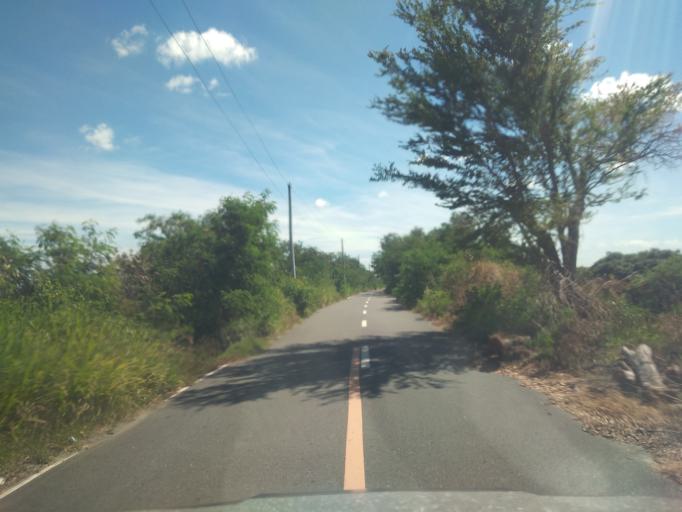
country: PH
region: Central Luzon
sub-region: Province of Pampanga
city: Balas
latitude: 15.0510
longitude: 120.5844
